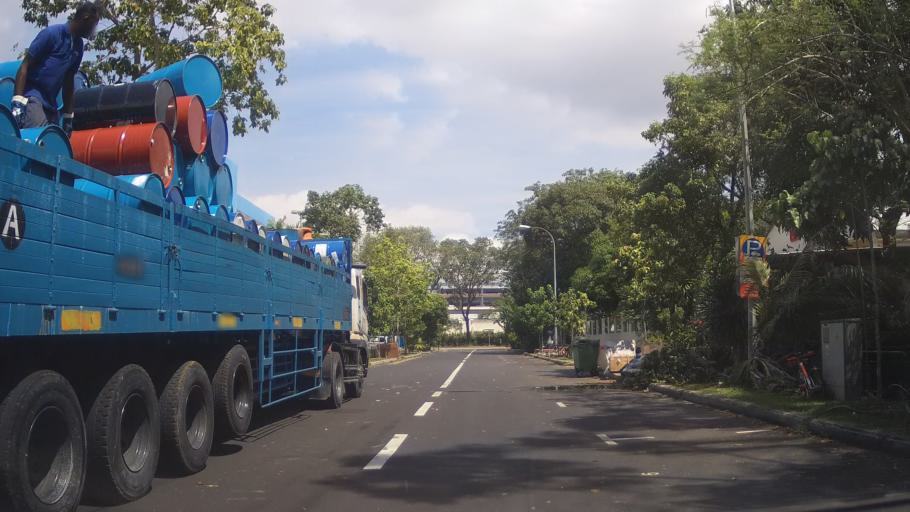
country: SG
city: Singapore
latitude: 1.3286
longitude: 103.7158
